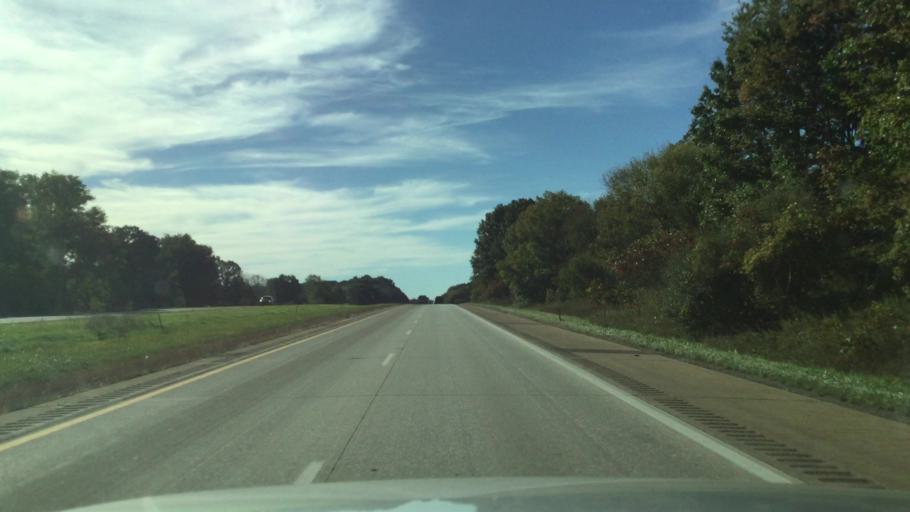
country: US
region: Michigan
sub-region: Calhoun County
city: Albion
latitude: 42.2622
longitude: -84.6705
